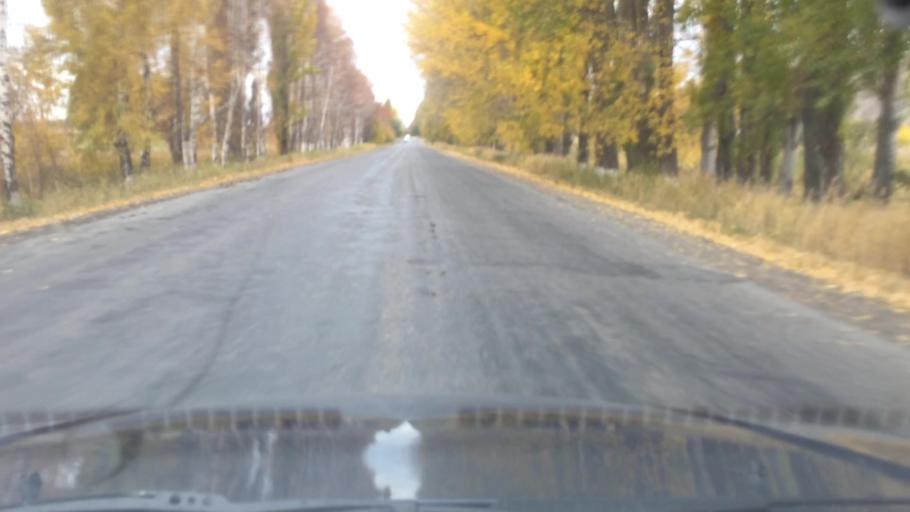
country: KG
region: Ysyk-Koel
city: Tyup
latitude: 42.7605
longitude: 78.1614
